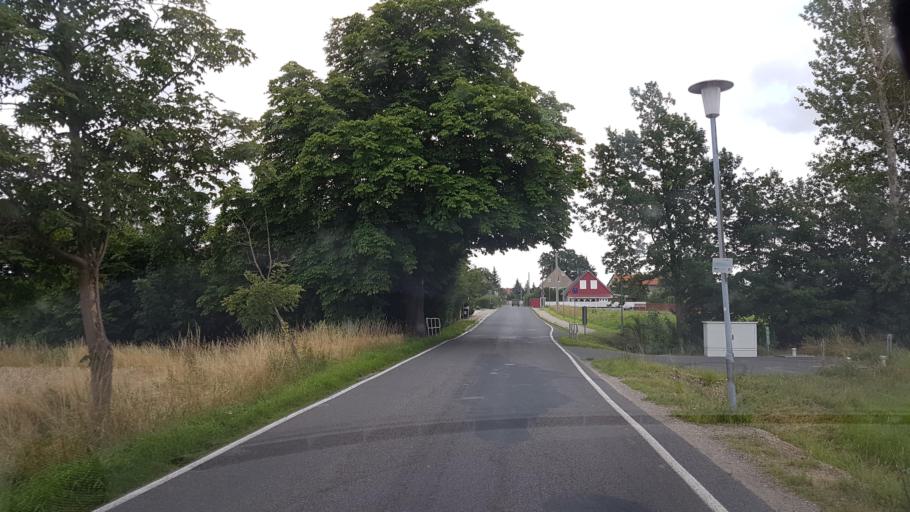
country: DE
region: Saxony
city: Priestewitz
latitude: 51.2637
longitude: 13.4906
